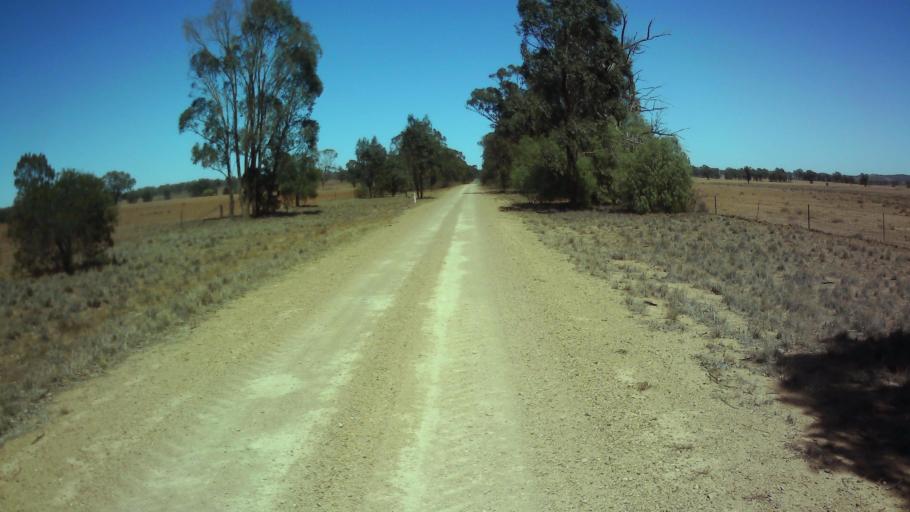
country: AU
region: New South Wales
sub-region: Forbes
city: Forbes
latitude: -33.6940
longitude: 147.8148
